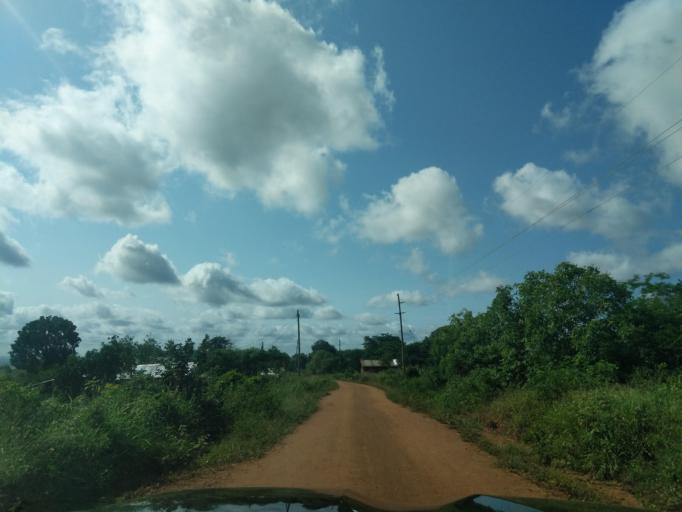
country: TZ
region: Tanga
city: Muheza
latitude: -5.4212
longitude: 38.6317
